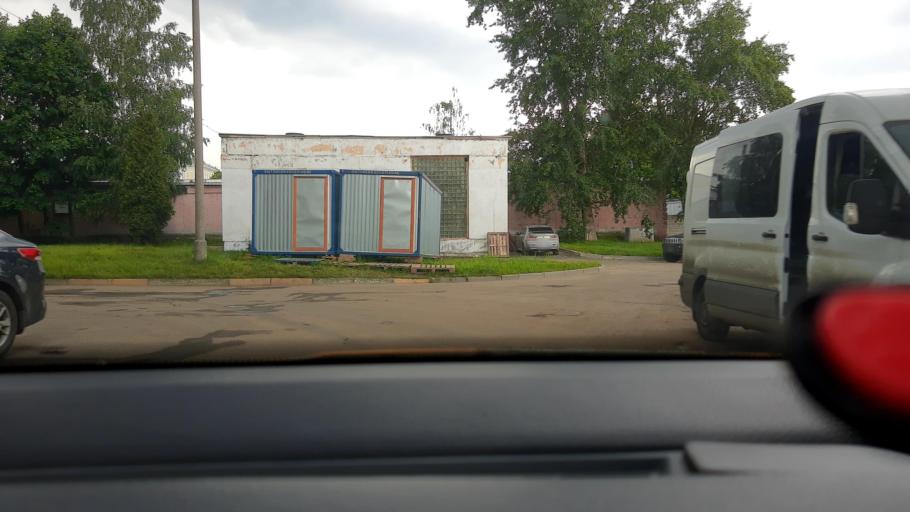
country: RU
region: Moscow
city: Lefortovo
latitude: 55.7716
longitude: 37.7384
